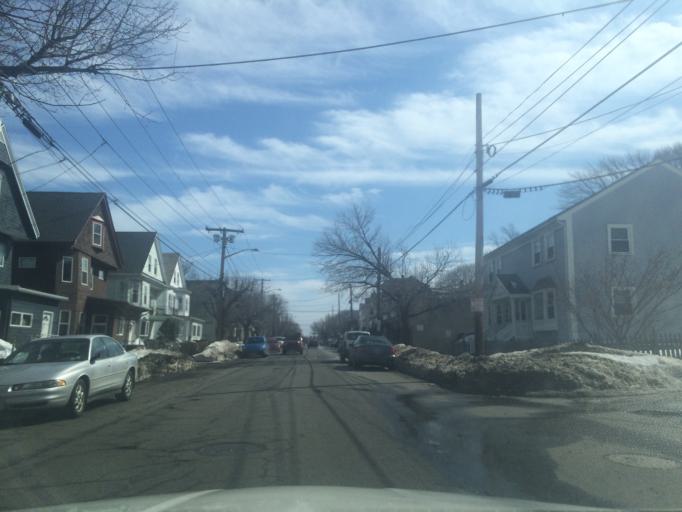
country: US
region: Massachusetts
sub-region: Middlesex County
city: Medford
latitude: 42.4134
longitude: -71.1246
